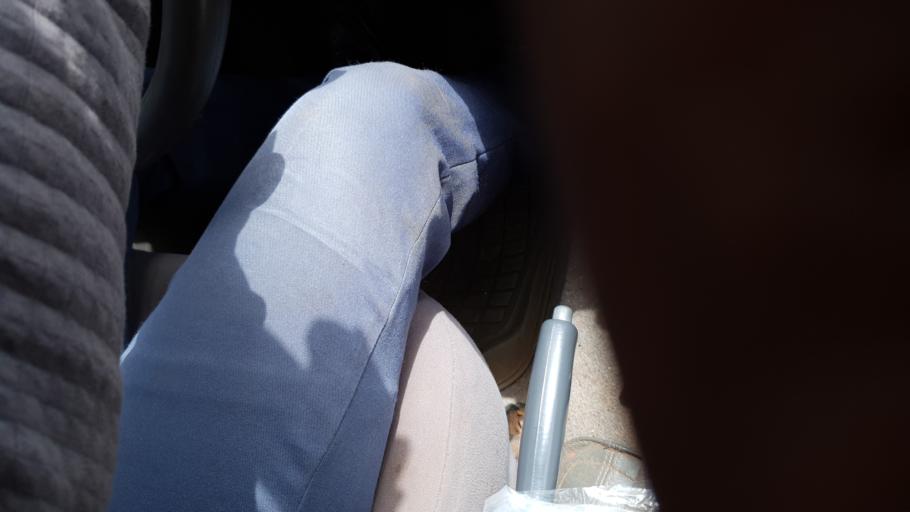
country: ML
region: Koulikoro
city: Kolokani
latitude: 13.3223
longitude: -8.2741
